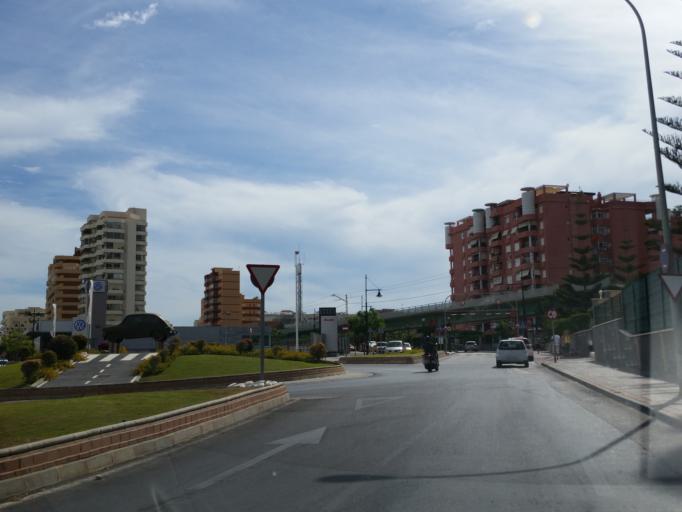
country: ES
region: Andalusia
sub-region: Provincia de Malaga
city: Fuengirola
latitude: 36.5580
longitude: -4.6115
